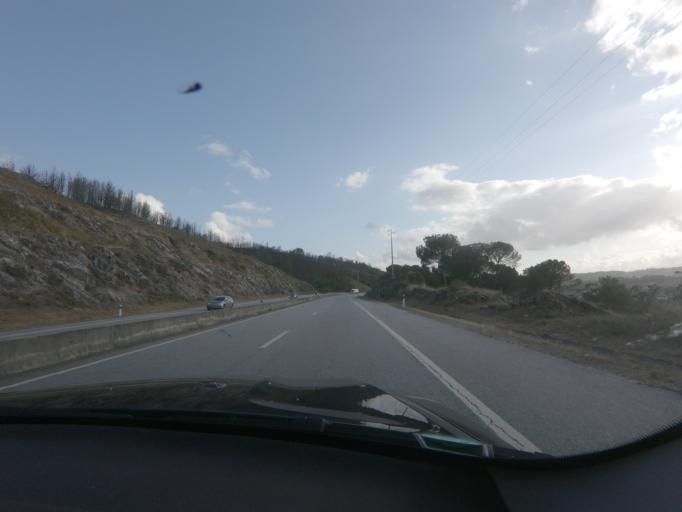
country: PT
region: Viseu
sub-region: Viseu
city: Viseu
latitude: 40.6101
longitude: -7.9675
